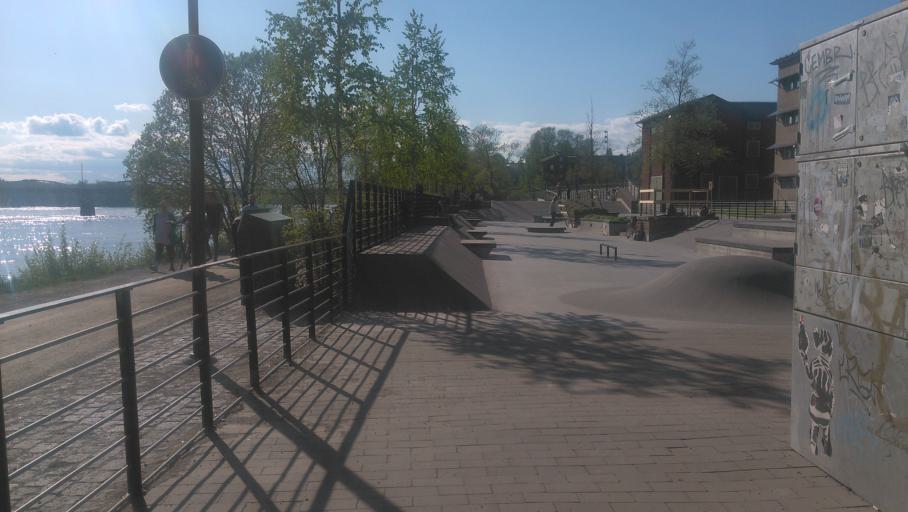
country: SE
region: Vaesterbotten
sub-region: Umea Kommun
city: Umea
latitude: 63.8252
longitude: 20.2552
